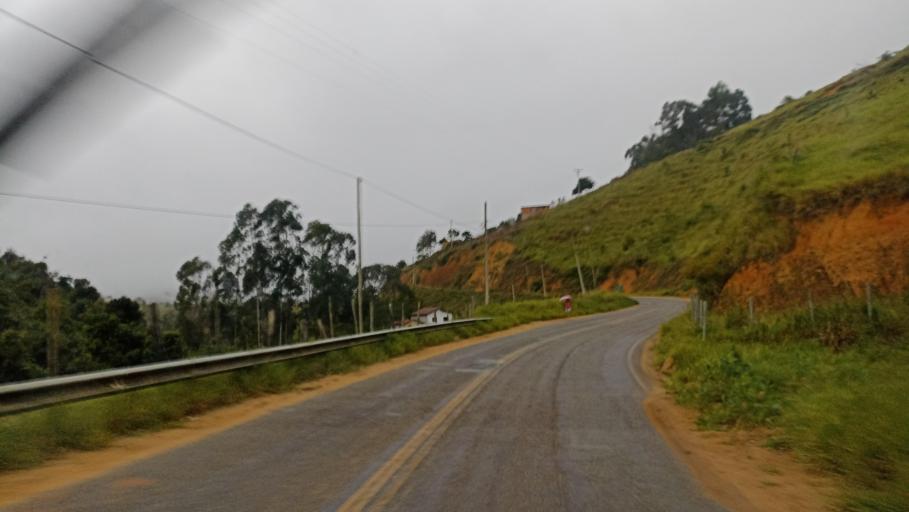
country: BR
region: Bahia
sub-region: Itanhem
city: Itanhem
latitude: -16.7351
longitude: -40.4314
